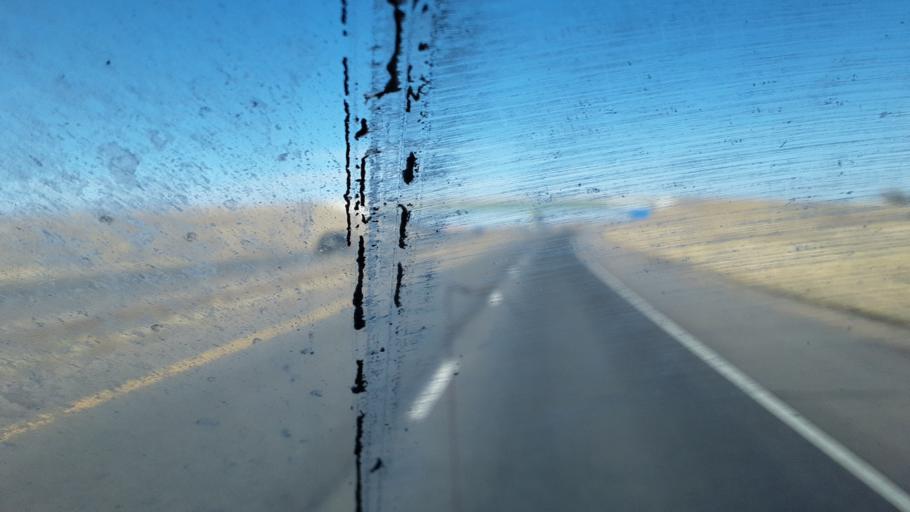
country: US
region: Colorado
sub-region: Weld County
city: Lochbuie
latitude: 39.9853
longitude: -104.7376
